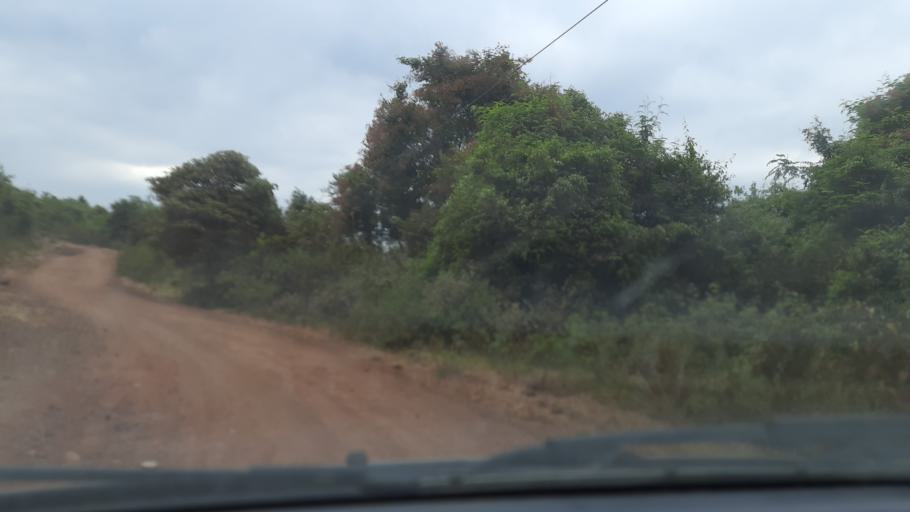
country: TZ
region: Kilimanjaro
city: Moshi
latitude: -2.8595
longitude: 37.2619
